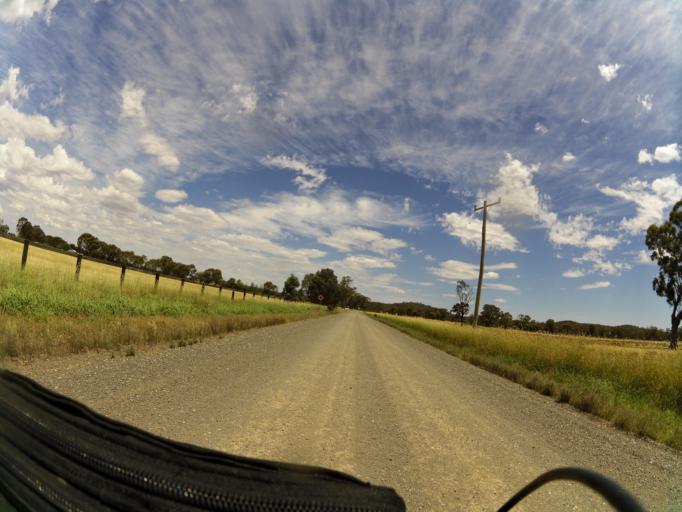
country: AU
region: Victoria
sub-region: Campaspe
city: Kyabram
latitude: -36.7570
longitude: 145.1029
